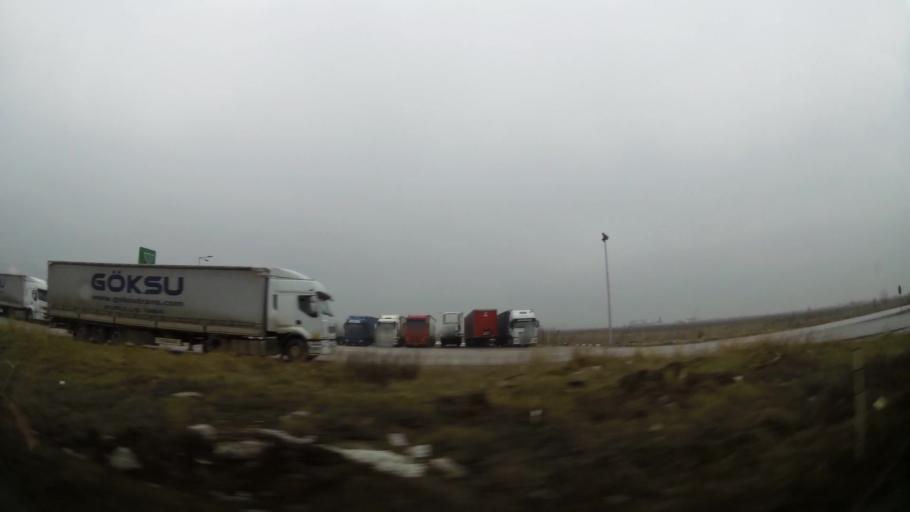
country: MK
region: Cucer-Sandevo
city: Chucher - Sandevo
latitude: 42.0591
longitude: 21.3761
